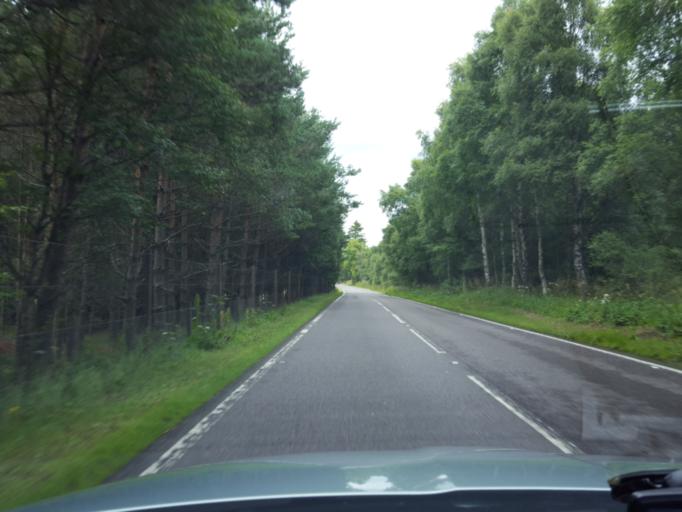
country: GB
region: Scotland
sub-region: Highland
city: Grantown on Spey
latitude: 57.3838
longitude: -3.4652
